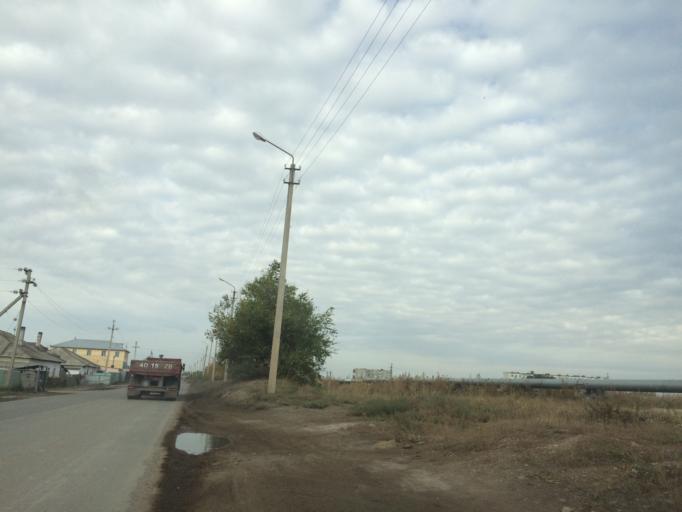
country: KZ
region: Astana Qalasy
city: Astana
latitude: 51.2067
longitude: 71.4114
